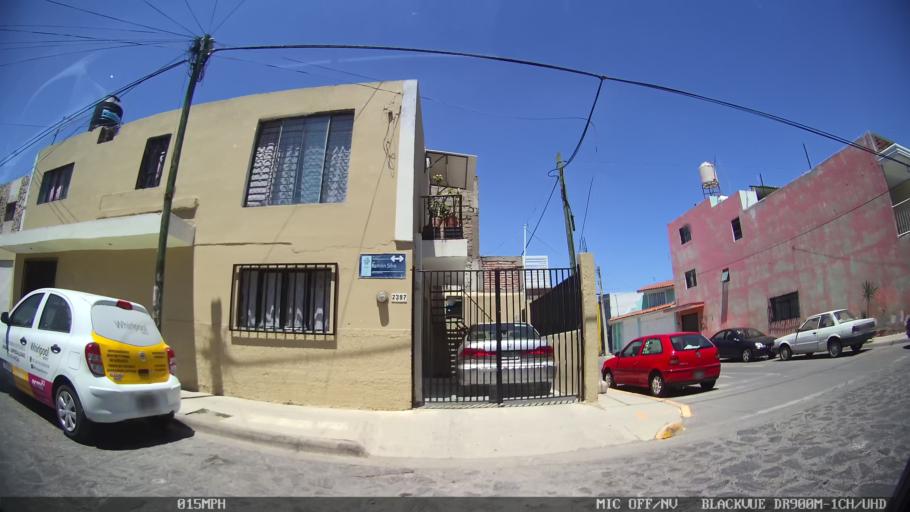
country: MX
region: Jalisco
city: Tlaquepaque
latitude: 20.6843
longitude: -103.2789
